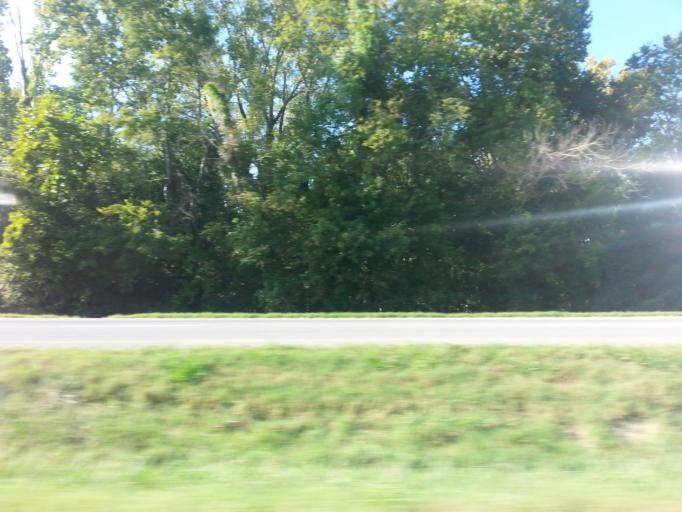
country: US
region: Alabama
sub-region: Colbert County
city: Tuscumbia
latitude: 34.7152
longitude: -87.7004
